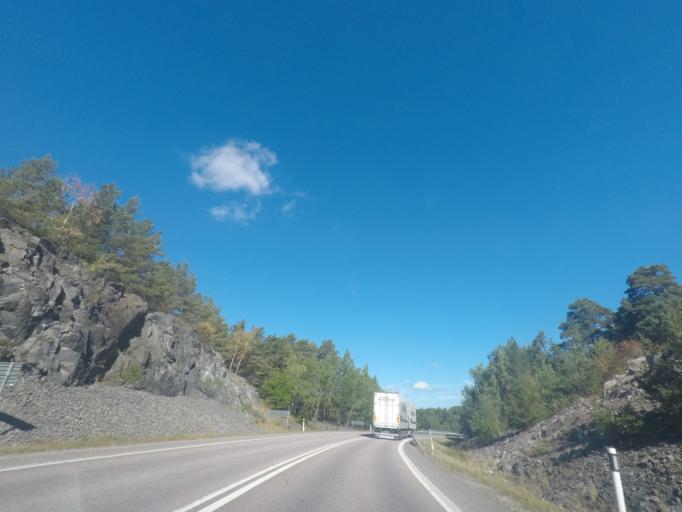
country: SE
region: Soedermanland
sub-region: Strangnas Kommun
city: Strangnas
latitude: 59.3773
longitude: 16.9843
